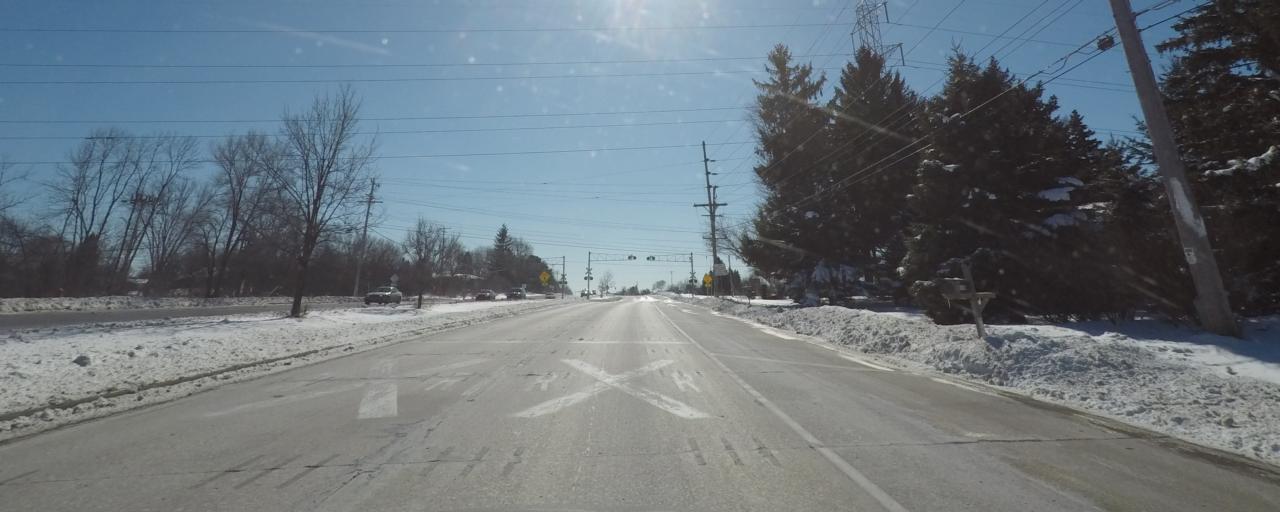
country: US
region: Wisconsin
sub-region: Waukesha County
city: New Berlin
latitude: 43.0109
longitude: -88.1076
